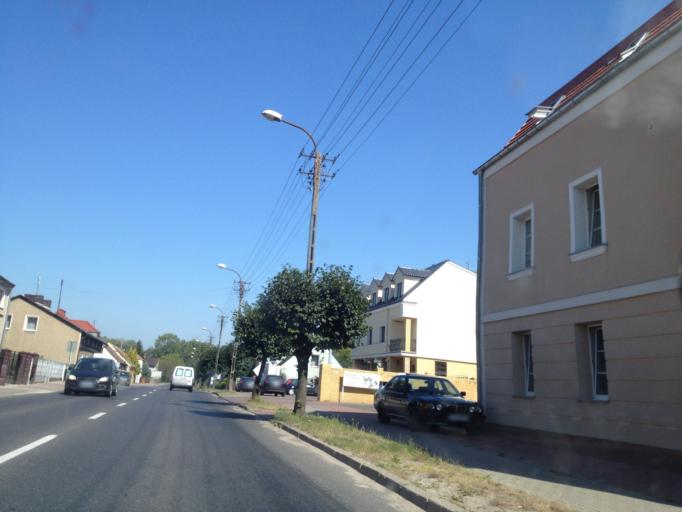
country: PL
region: Greater Poland Voivodeship
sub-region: Powiat poznanski
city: Kornik
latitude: 52.2342
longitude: 17.0950
